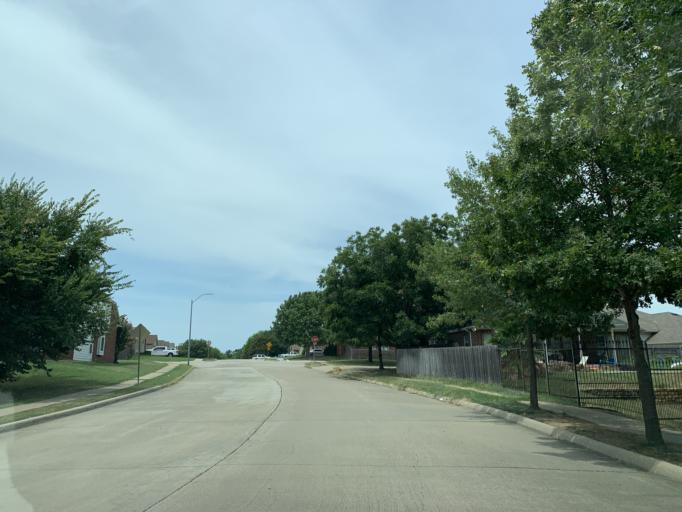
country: US
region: Texas
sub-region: Dallas County
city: Grand Prairie
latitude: 32.6645
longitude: -97.0192
